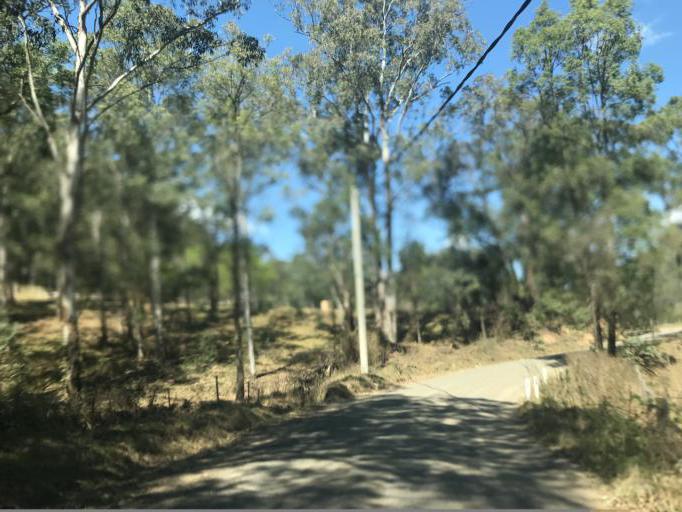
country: AU
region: New South Wales
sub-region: Hornsby Shire
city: Glenorie
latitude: -33.2795
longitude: 150.9687
